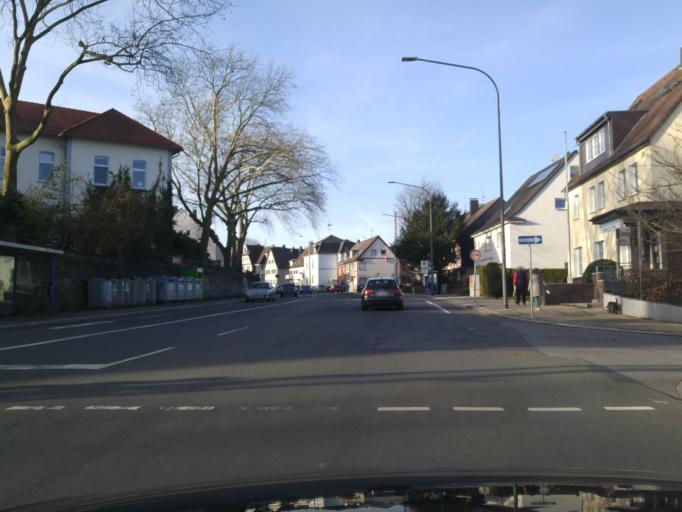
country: DE
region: North Rhine-Westphalia
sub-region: Regierungsbezirk Dusseldorf
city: Essen
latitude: 51.4241
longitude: 7.0355
